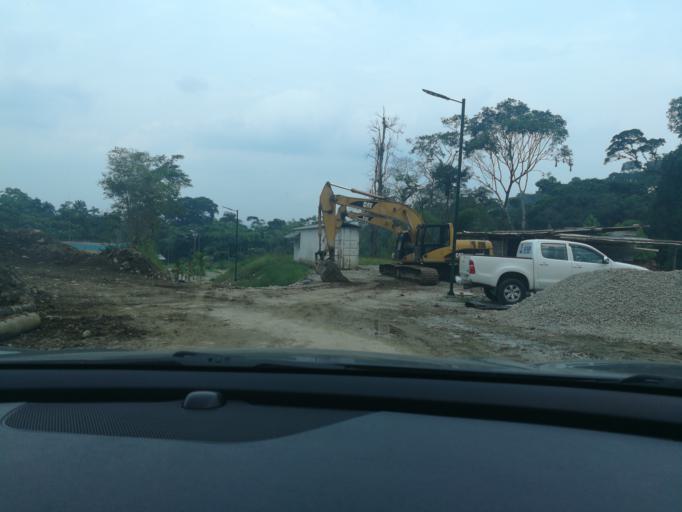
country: EC
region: Napo
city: Archidona
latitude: -0.9461
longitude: -77.8920
